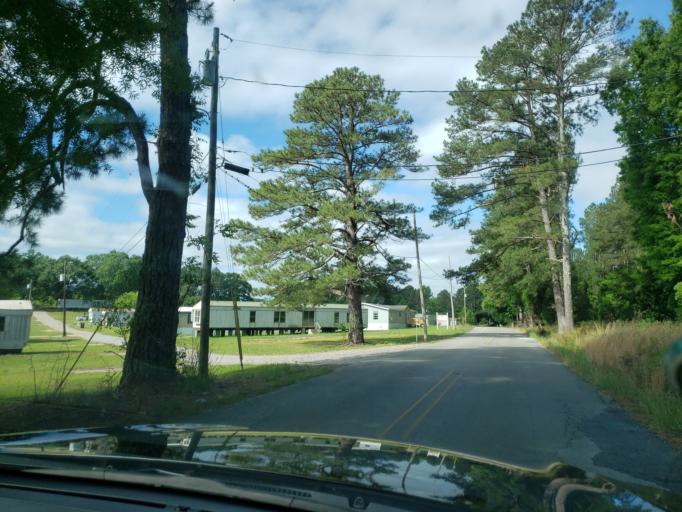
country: US
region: Alabama
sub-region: Calhoun County
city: Weaver
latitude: 33.7561
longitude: -85.8263
